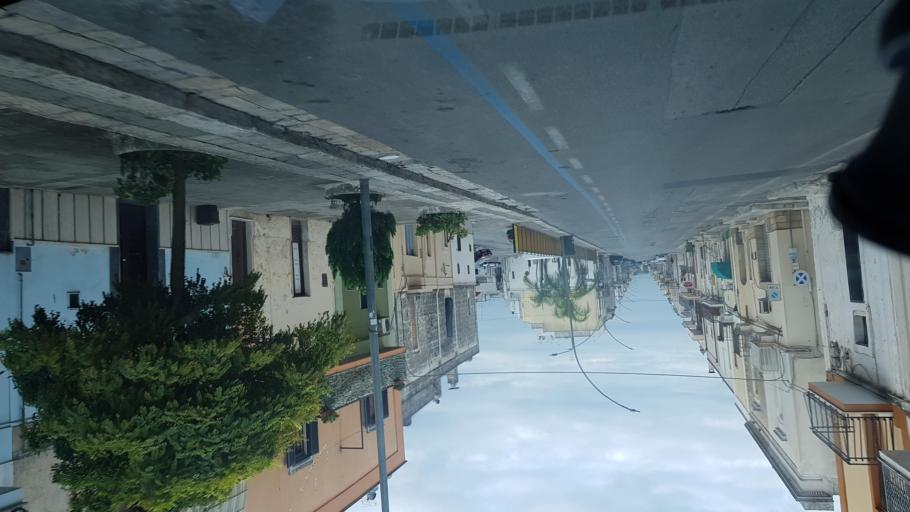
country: IT
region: Apulia
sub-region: Provincia di Brindisi
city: Oria
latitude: 40.4961
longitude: 17.6456
